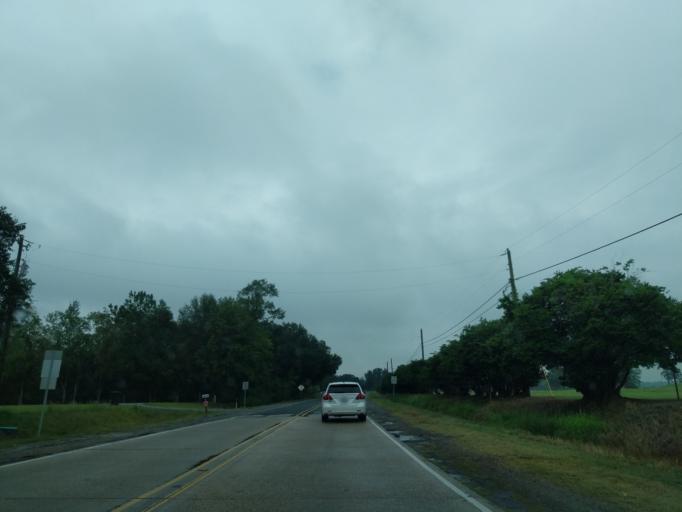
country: US
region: Louisiana
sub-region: Vermilion Parish
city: Abbeville
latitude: 29.9856
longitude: -92.1574
